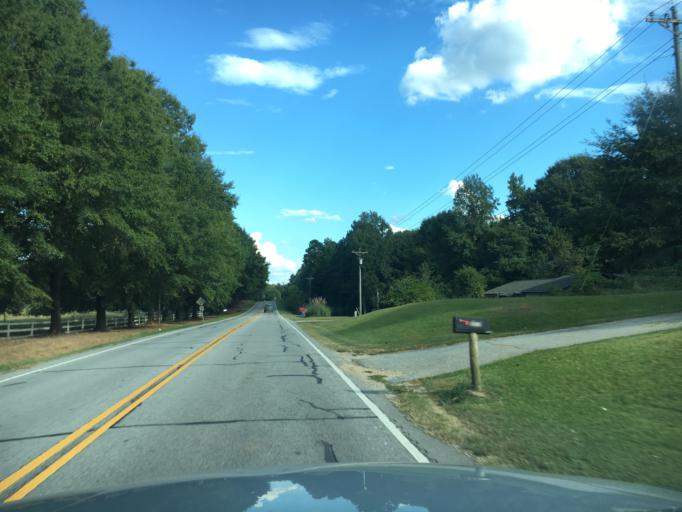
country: US
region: South Carolina
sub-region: Laurens County
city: Laurens
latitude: 34.5210
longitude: -82.1137
